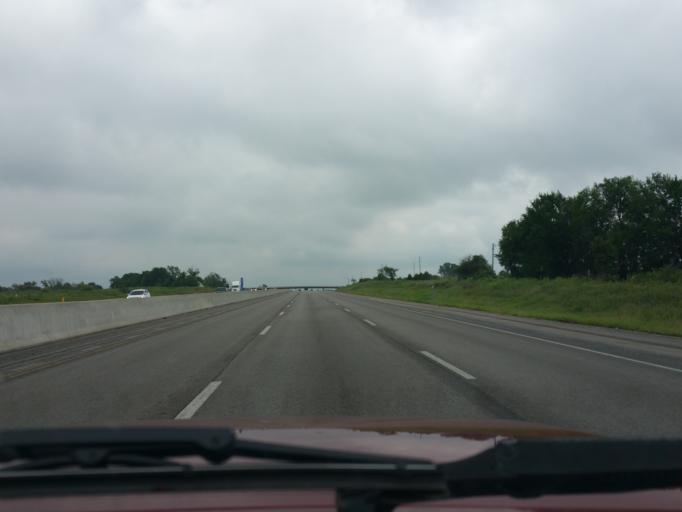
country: US
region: Kansas
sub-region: Douglas County
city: Lawrence
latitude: 39.0083
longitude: -95.4546
